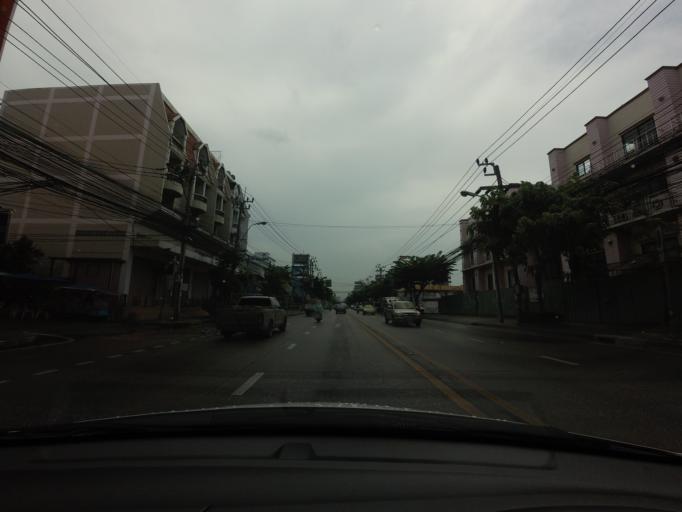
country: TH
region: Bangkok
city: Suan Luang
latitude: 13.7108
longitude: 100.6353
